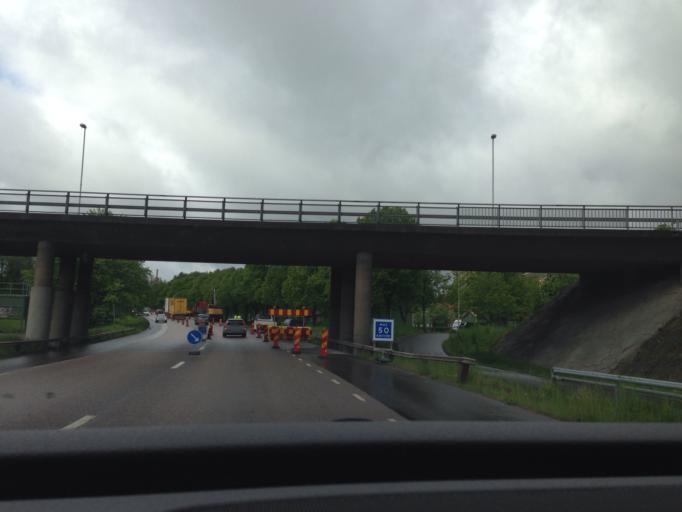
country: SE
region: Vaestra Goetaland
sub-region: Skovde Kommun
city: Skoevde
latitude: 58.3929
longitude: 13.8350
